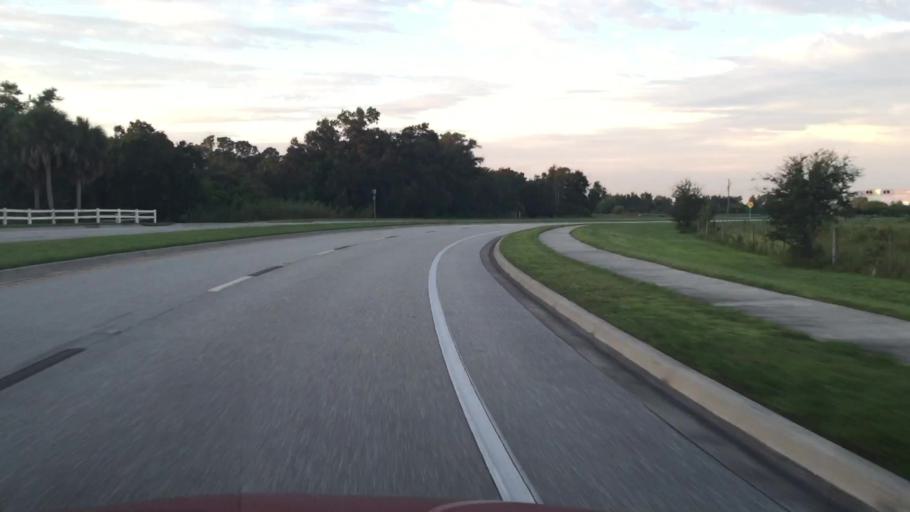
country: US
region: Florida
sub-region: Lee County
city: Estero
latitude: 26.4249
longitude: -81.8041
